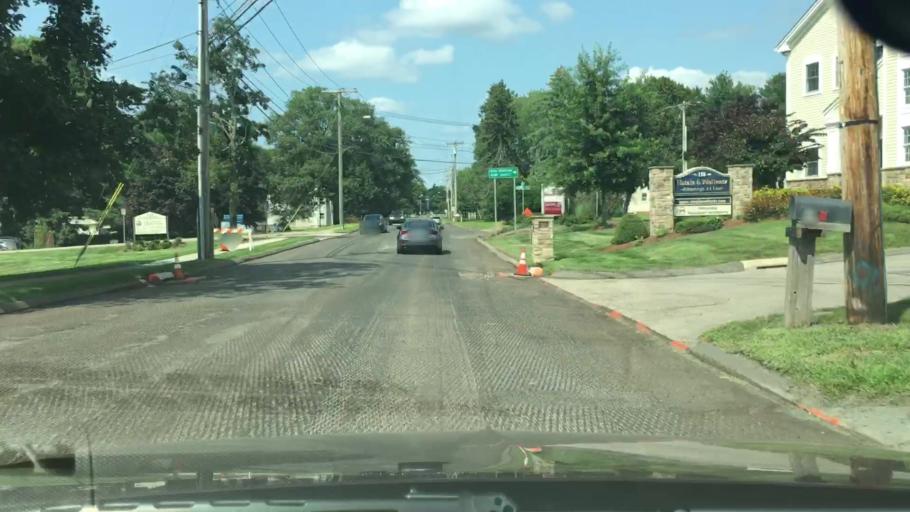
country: US
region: Connecticut
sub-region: Hartford County
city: Glastonbury Center
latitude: 41.7087
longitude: -72.5922
